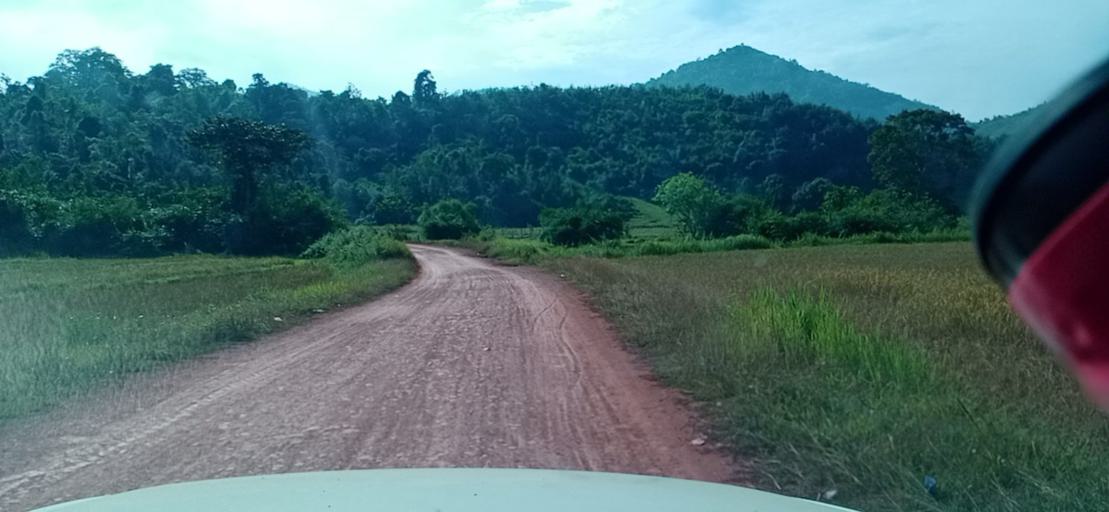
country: TH
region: Changwat Bueng Kan
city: Pak Khat
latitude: 18.6742
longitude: 103.1953
